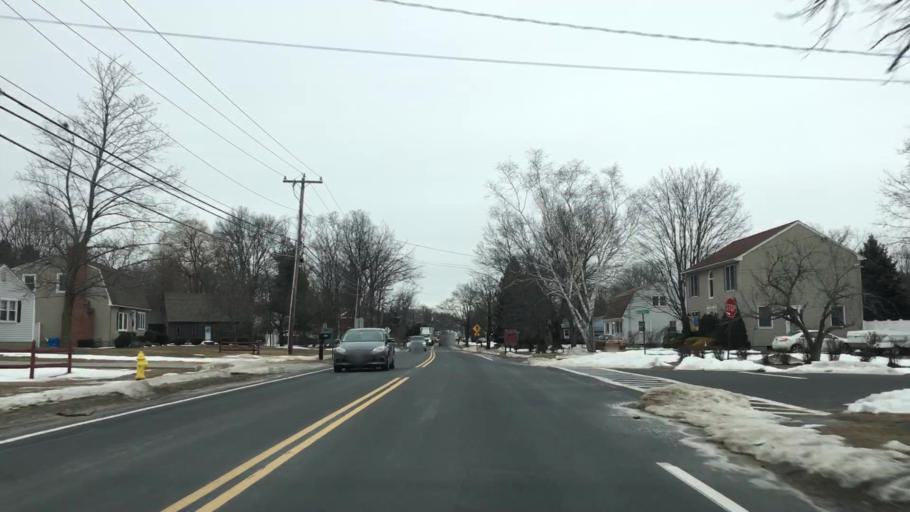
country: US
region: Massachusetts
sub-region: Hampden County
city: Agawam
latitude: 42.0730
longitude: -72.6783
